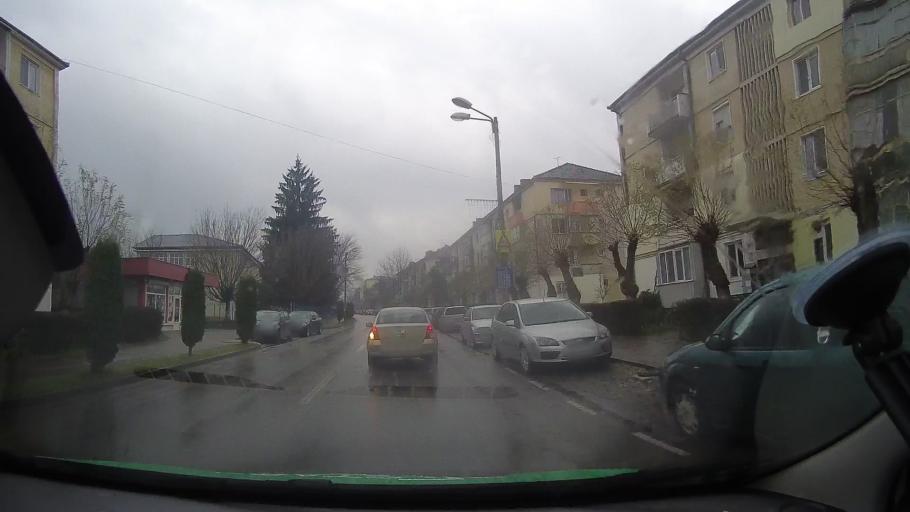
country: RO
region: Hunedoara
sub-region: Municipiul Brad
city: Brad
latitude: 46.1233
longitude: 22.7909
